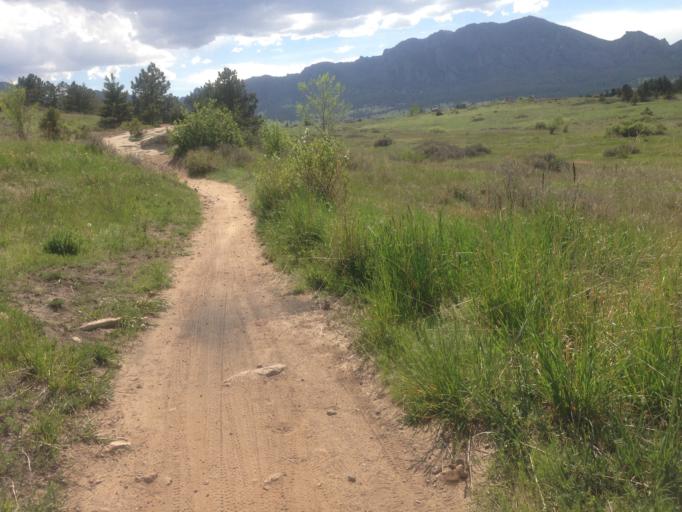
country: US
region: Colorado
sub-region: Boulder County
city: Superior
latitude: 39.9528
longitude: -105.2251
